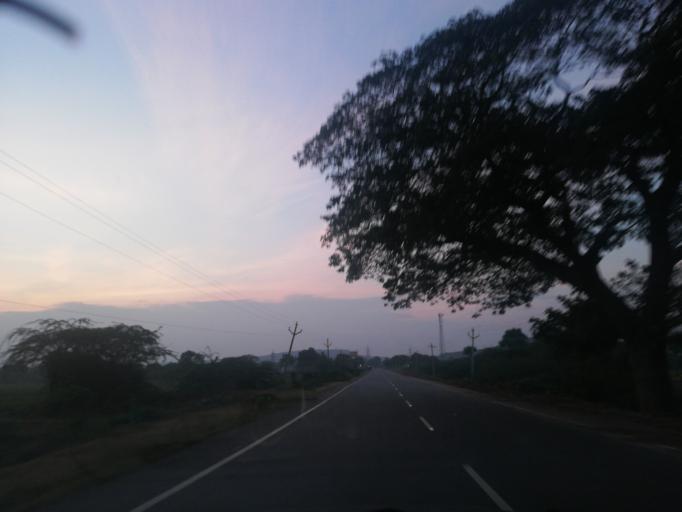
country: IN
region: Andhra Pradesh
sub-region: Guntur
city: Macherla
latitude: 16.6790
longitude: 79.2626
